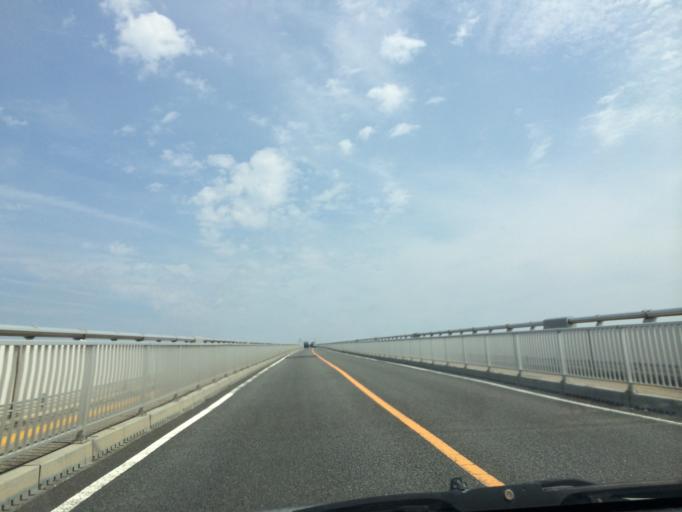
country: JP
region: Shimane
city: Sakaiminato
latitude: 35.5167
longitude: 133.1941
